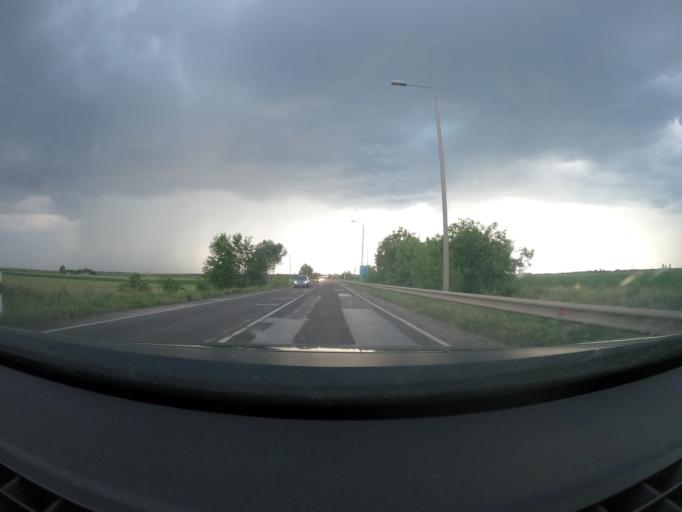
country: HU
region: Hajdu-Bihar
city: Ebes
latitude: 47.4985
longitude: 21.5547
